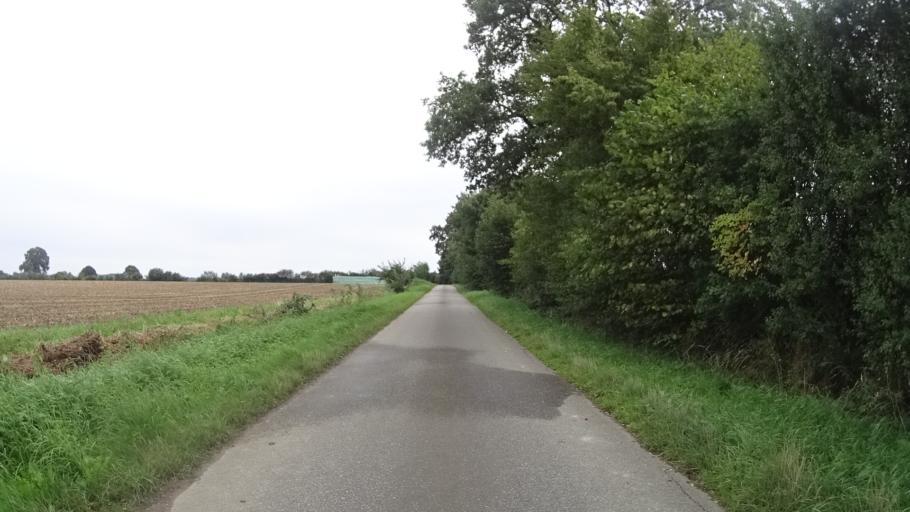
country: DE
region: Schleswig-Holstein
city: Schiphorst
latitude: 53.7131
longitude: 10.4522
